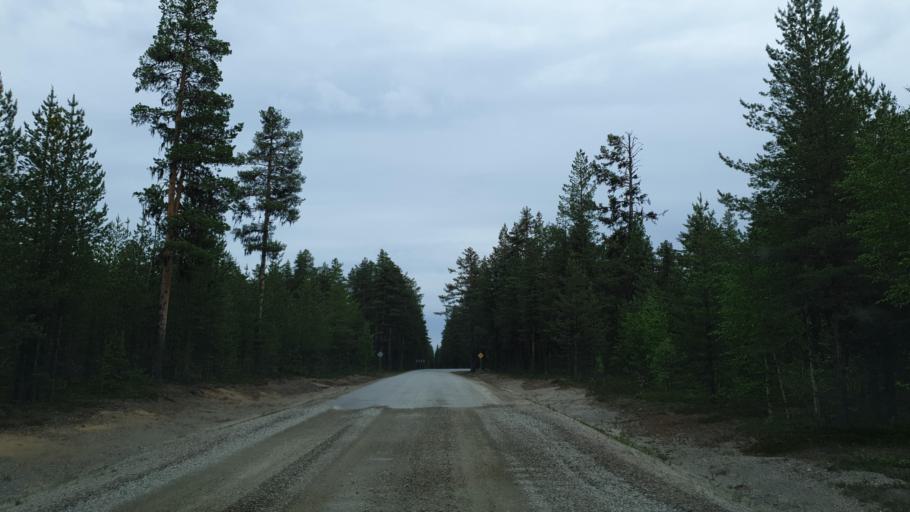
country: SE
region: Vaesterbotten
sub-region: Sorsele Kommun
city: Sorsele
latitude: 65.5523
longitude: 17.5077
